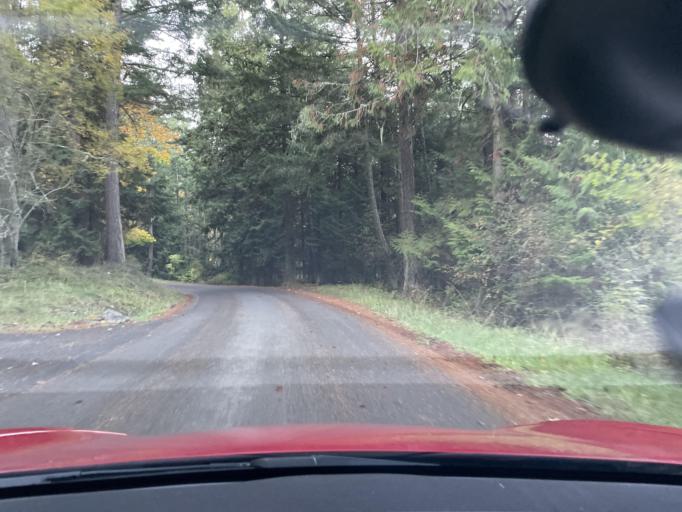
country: US
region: Washington
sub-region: San Juan County
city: Friday Harbor
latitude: 48.6007
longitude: -123.1509
